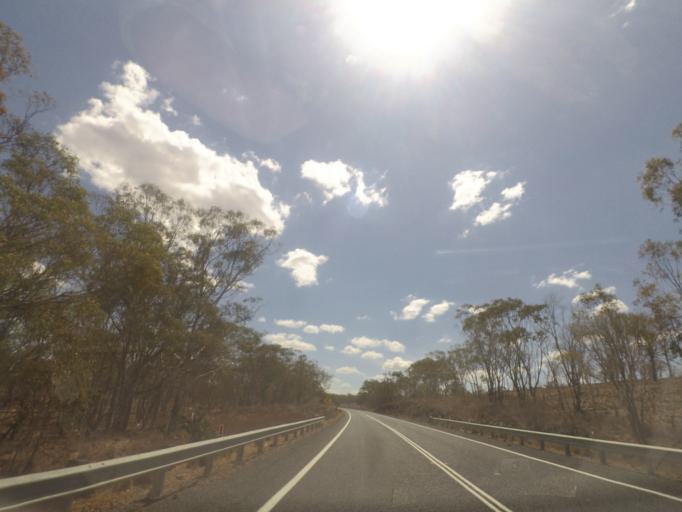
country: AU
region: Queensland
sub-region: Southern Downs
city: Warwick
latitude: -28.1607
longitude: 151.6913
